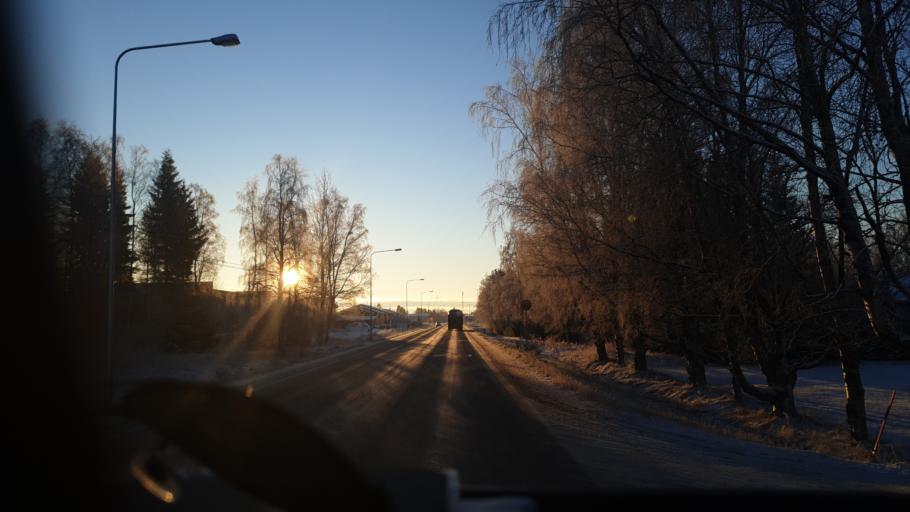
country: FI
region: Northern Ostrobothnia
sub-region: Ylivieska
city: Kalajoki
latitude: 64.2691
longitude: 23.9491
